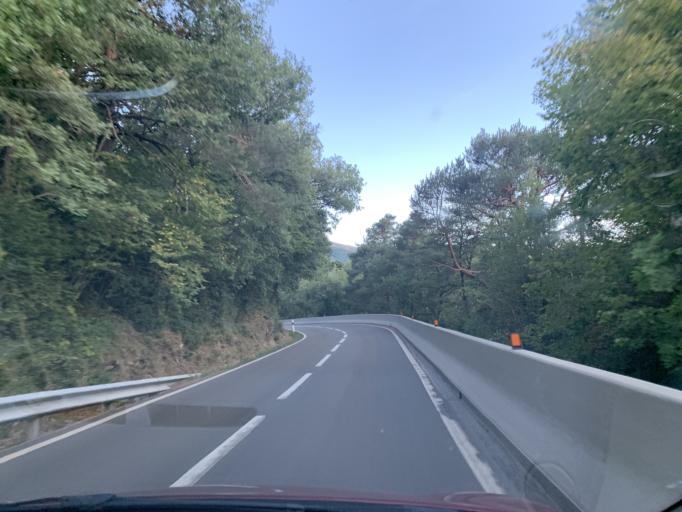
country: ES
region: Aragon
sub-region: Provincia de Huesca
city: Broto
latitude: 42.5824
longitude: -0.1154
